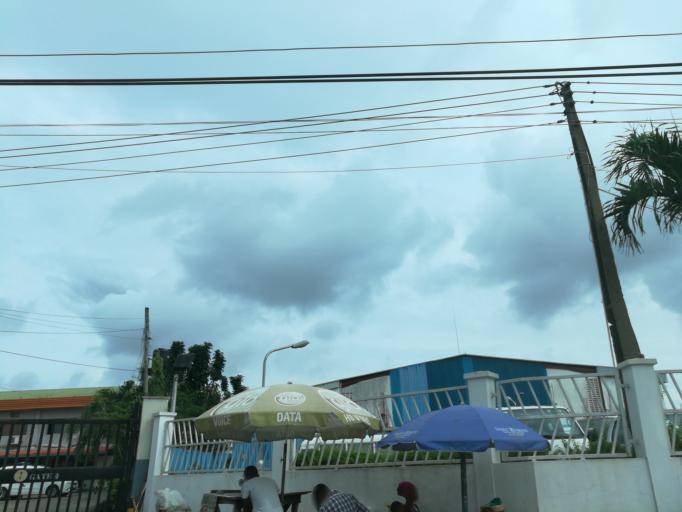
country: NG
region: Lagos
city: Ikeja
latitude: 6.5912
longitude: 3.3339
